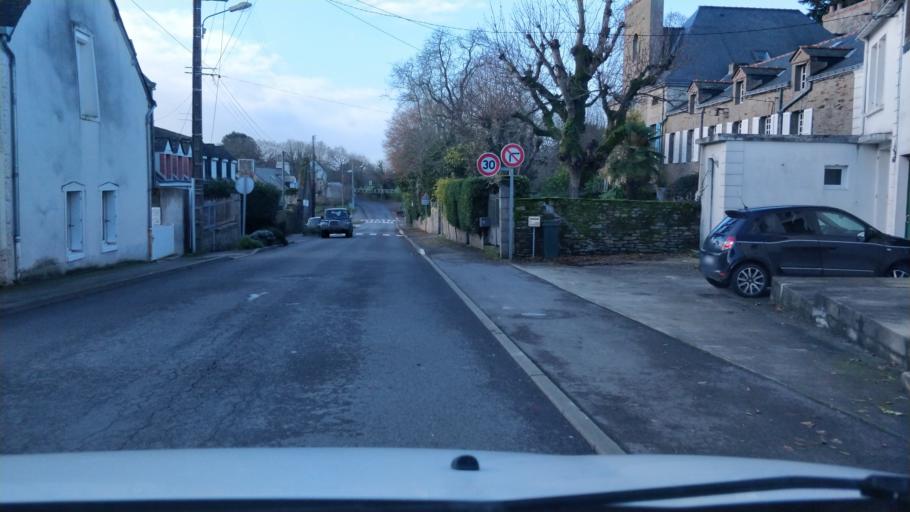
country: FR
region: Pays de la Loire
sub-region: Departement de la Loire-Atlantique
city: Asserac
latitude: 47.4286
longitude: -2.3913
